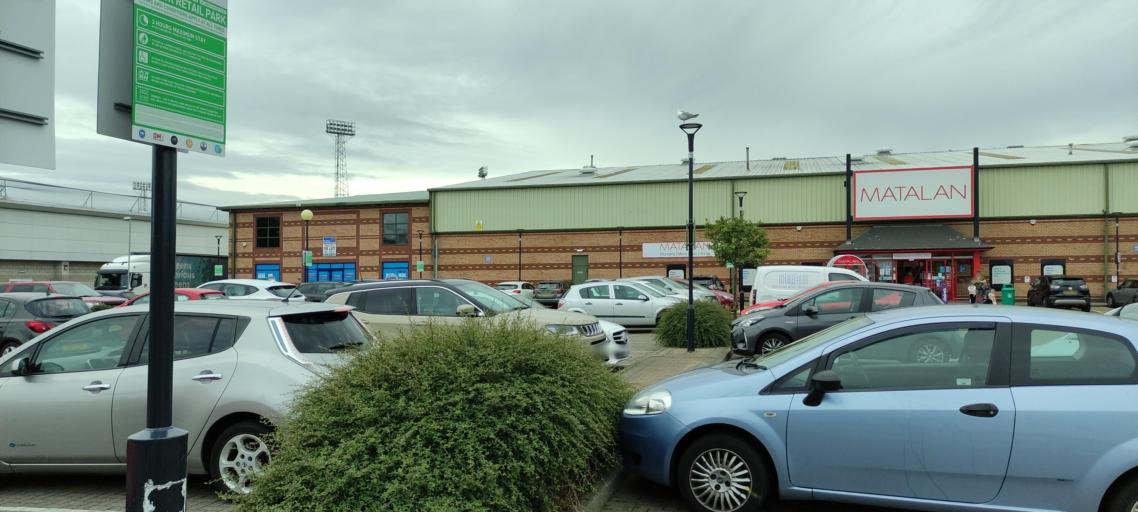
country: GB
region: England
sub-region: Hartlepool
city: Hartlepool
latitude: 54.6905
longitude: -1.2099
